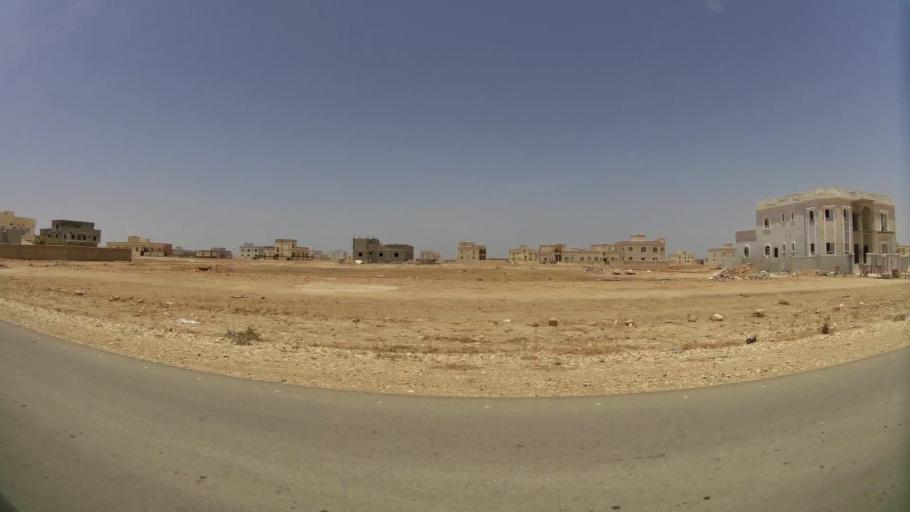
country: OM
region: Zufar
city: Salalah
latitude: 17.0976
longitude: 54.1783
